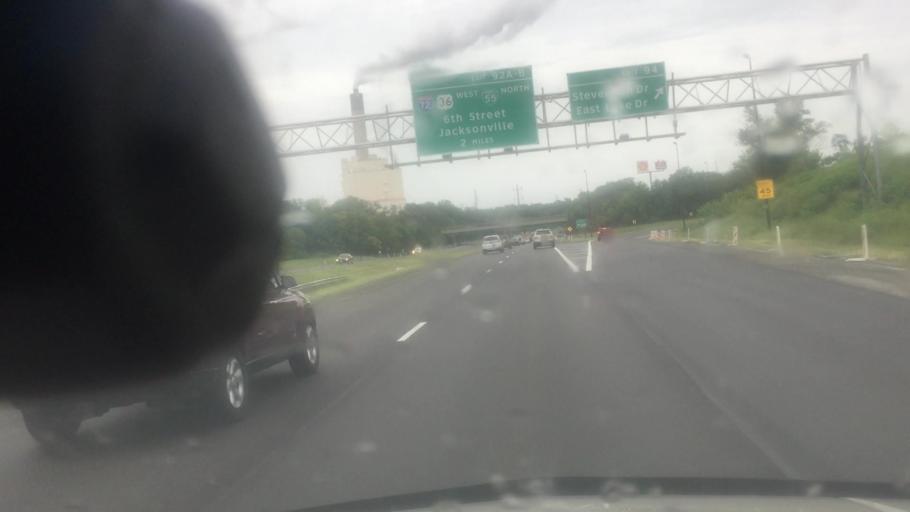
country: US
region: Illinois
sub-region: Sangamon County
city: Southern View
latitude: 39.7621
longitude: -89.6052
